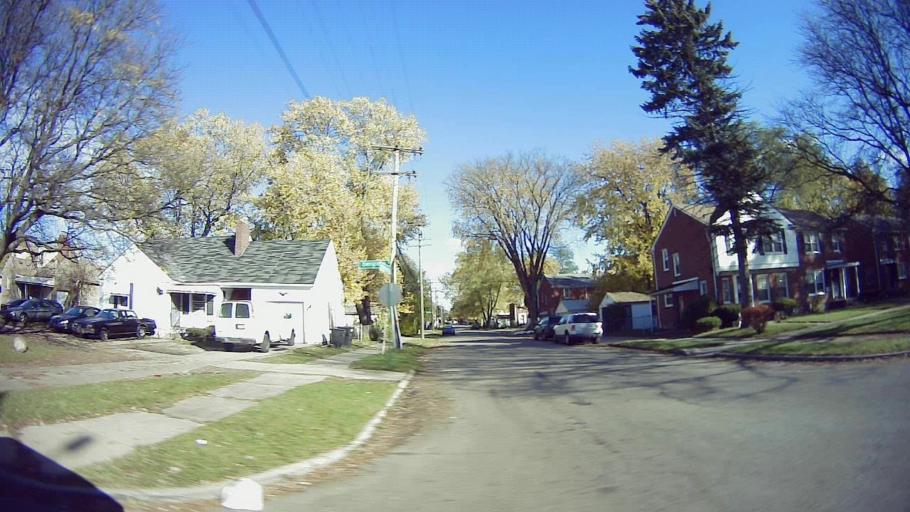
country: US
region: Michigan
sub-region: Oakland County
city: Southfield
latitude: 42.4224
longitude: -83.2385
